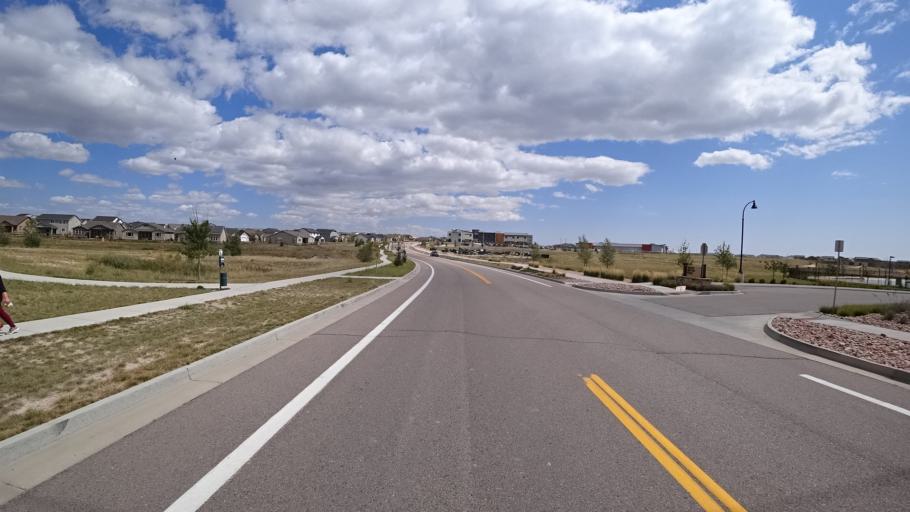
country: US
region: Colorado
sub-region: El Paso County
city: Cimarron Hills
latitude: 38.9331
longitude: -104.6636
